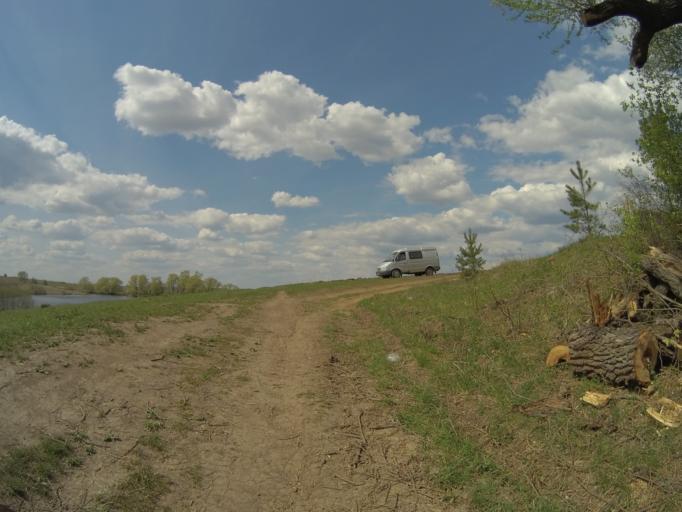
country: RU
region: Vladimir
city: Suzdal'
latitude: 56.3312
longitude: 40.3616
